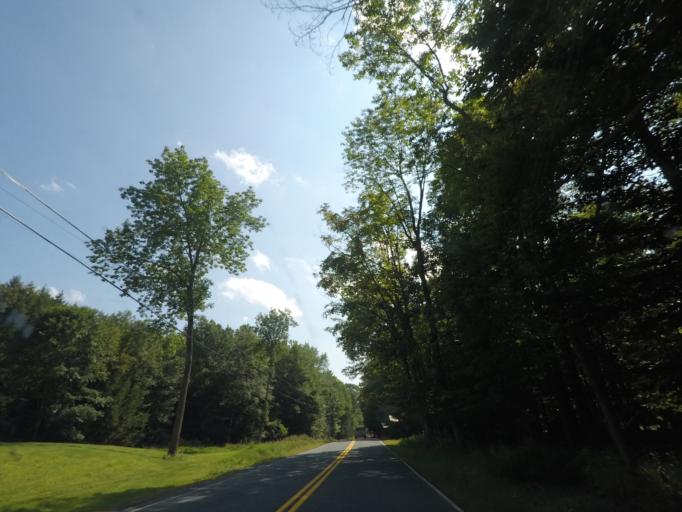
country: US
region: New York
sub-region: Rensselaer County
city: Poestenkill
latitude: 42.7054
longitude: -73.5131
